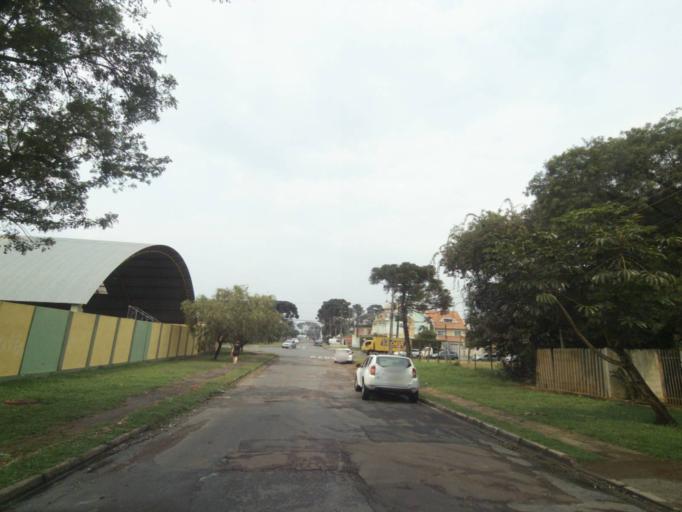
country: BR
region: Parana
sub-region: Curitiba
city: Curitiba
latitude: -25.4789
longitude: -49.3000
